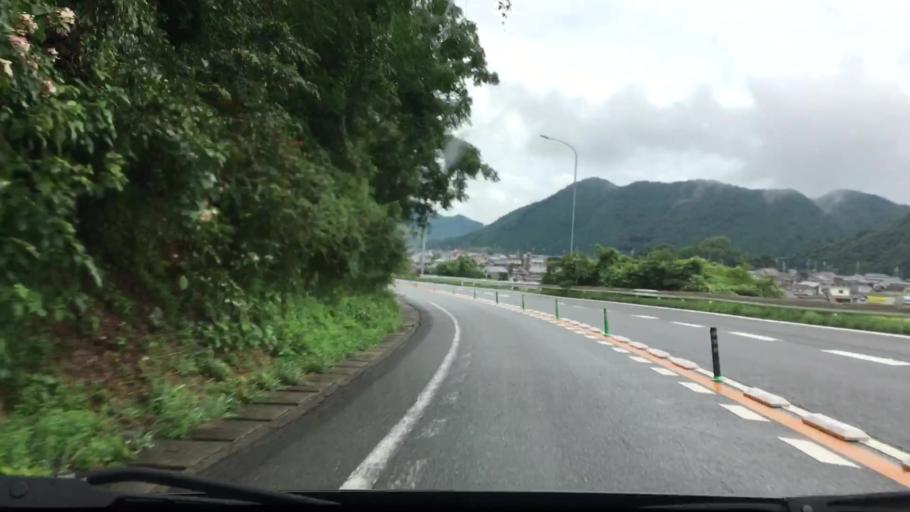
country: JP
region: Hyogo
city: Himeji
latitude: 35.0142
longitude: 134.7608
